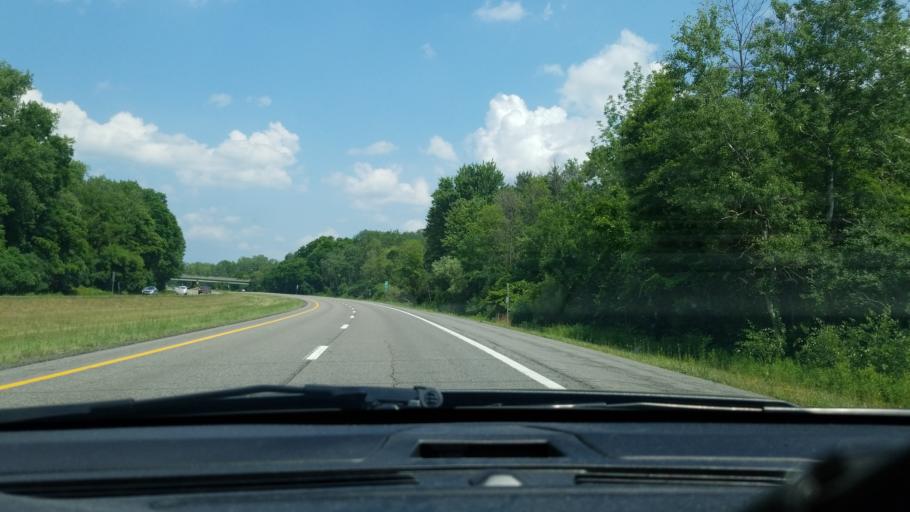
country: US
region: New York
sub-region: Onondaga County
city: Liverpool
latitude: 43.1707
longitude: -76.2032
